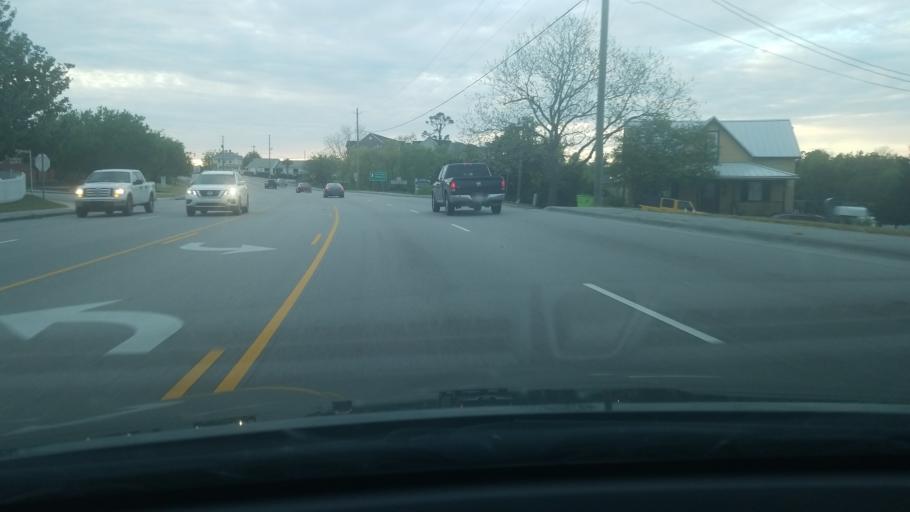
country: US
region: North Carolina
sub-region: Onslow County
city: Swansboro
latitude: 34.6883
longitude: -77.1182
